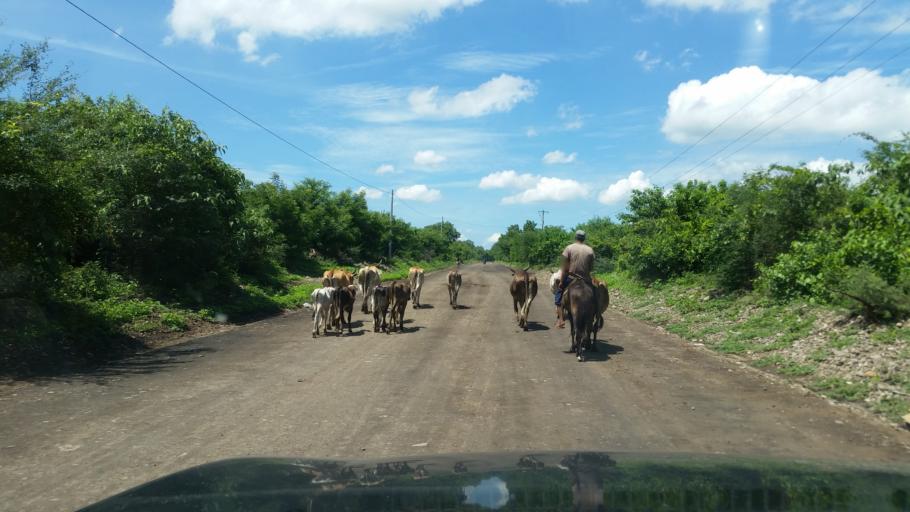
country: NI
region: Chinandega
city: El Viejo
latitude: 12.7527
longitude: -87.1338
